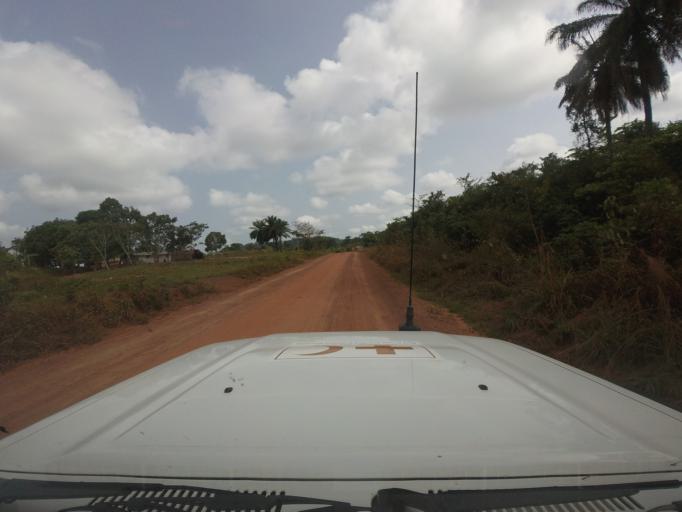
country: LR
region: Bong
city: Gbarnga
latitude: 7.2355
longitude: -9.4375
